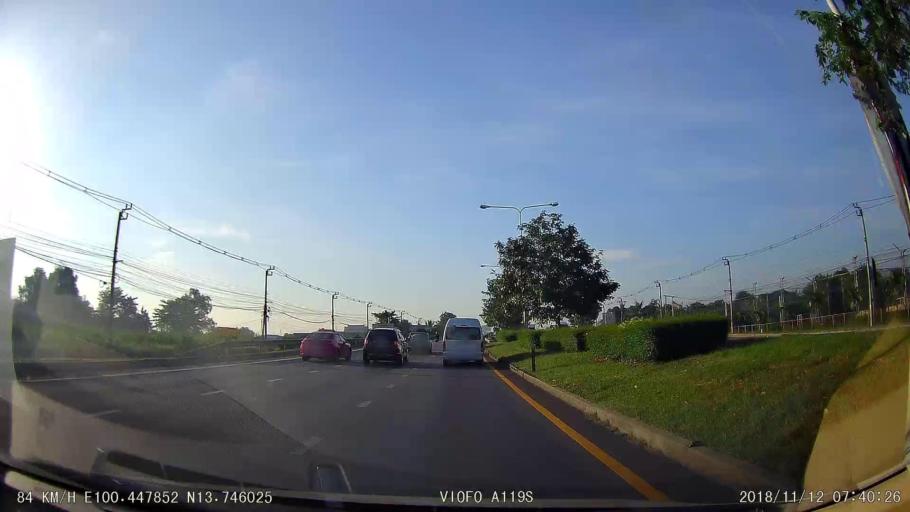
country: TH
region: Bangkok
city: Phasi Charoen
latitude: 13.7450
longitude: 100.4478
